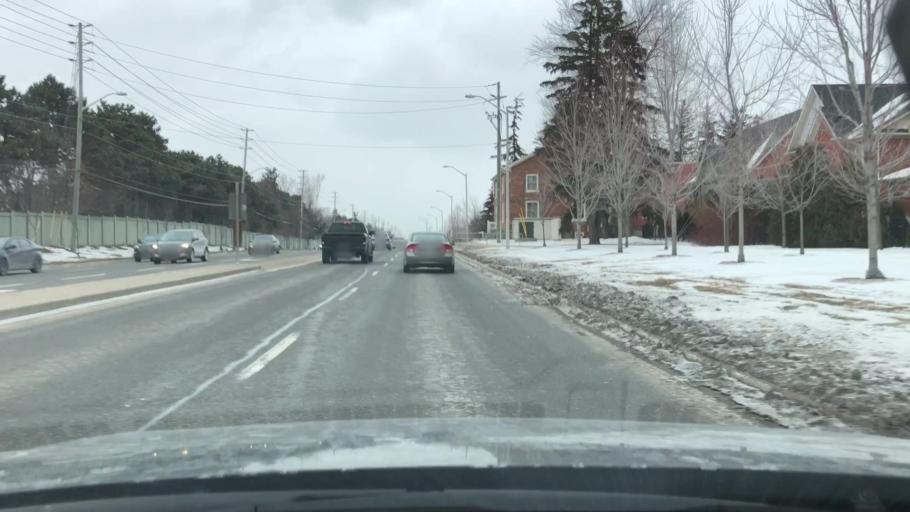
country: CA
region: Ontario
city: Markham
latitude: 43.8888
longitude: -79.2372
